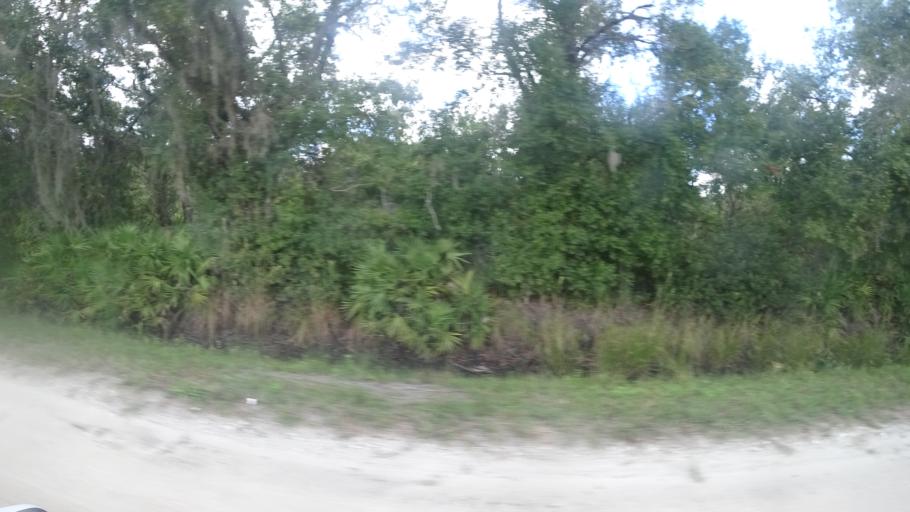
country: US
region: Florida
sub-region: Hillsborough County
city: Ruskin
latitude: 27.6349
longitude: -82.3966
